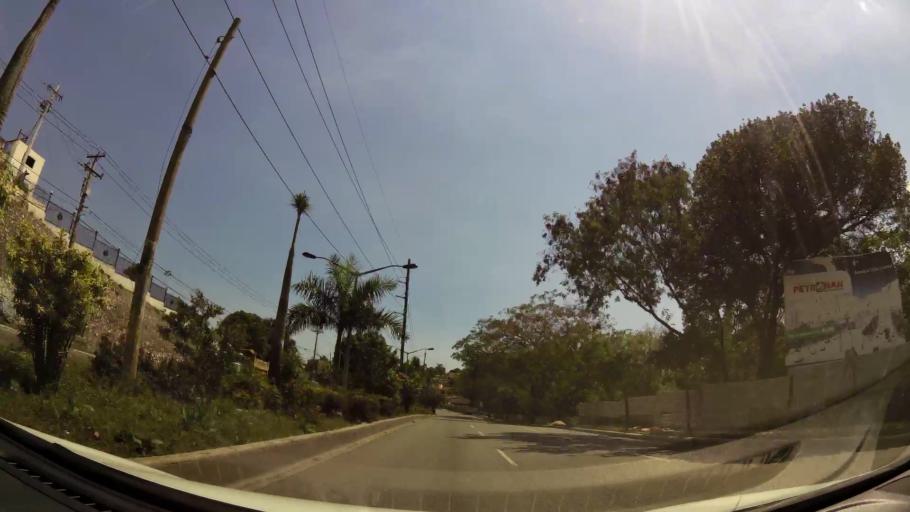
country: DO
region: Santo Domingo
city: Santo Domingo Oeste
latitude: 18.4792
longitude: -69.9975
